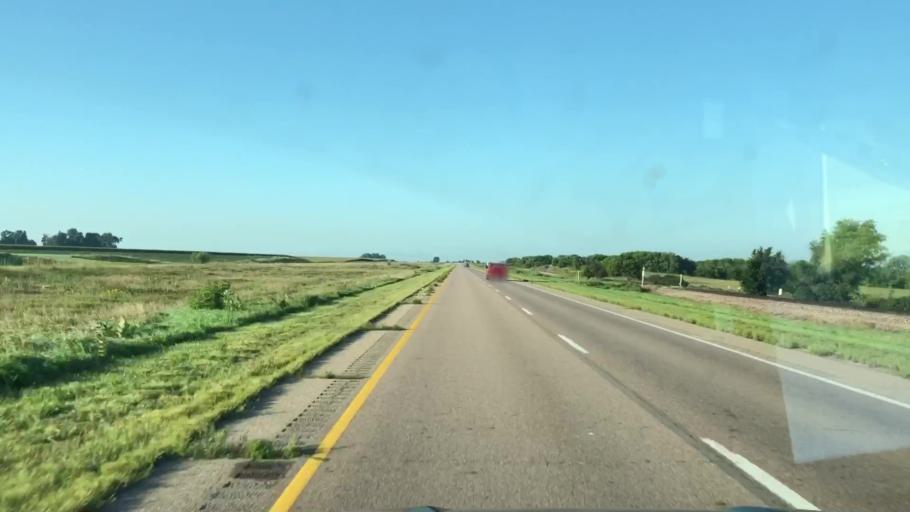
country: US
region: Iowa
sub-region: O'Brien County
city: Sheldon
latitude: 43.1199
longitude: -95.8907
